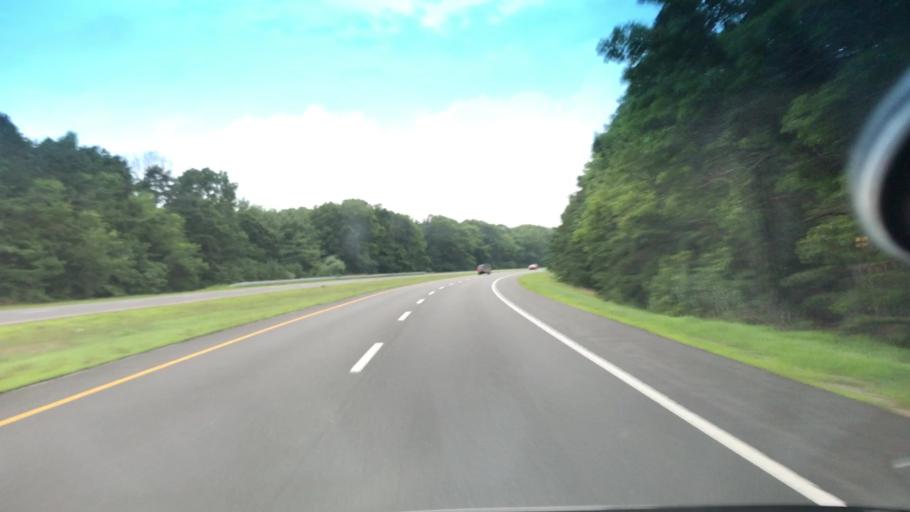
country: US
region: New York
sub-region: Suffolk County
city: Yaphank
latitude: 40.8543
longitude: -72.8993
